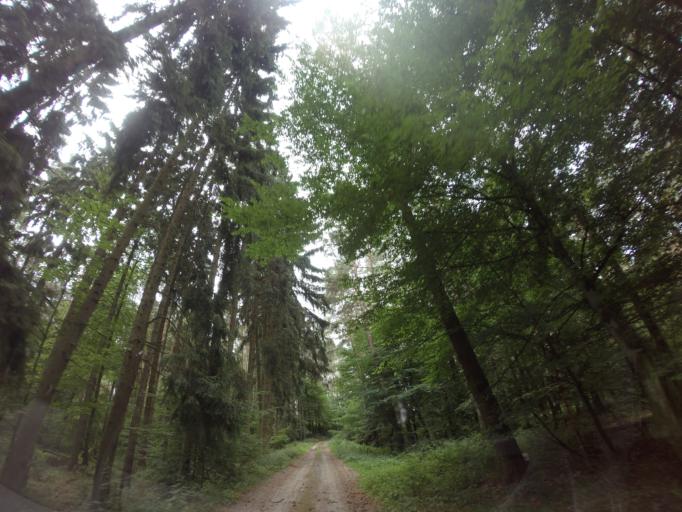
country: PL
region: Lubusz
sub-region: Powiat strzelecko-drezdenecki
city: Strzelce Krajenskie
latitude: 52.9275
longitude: 15.6081
